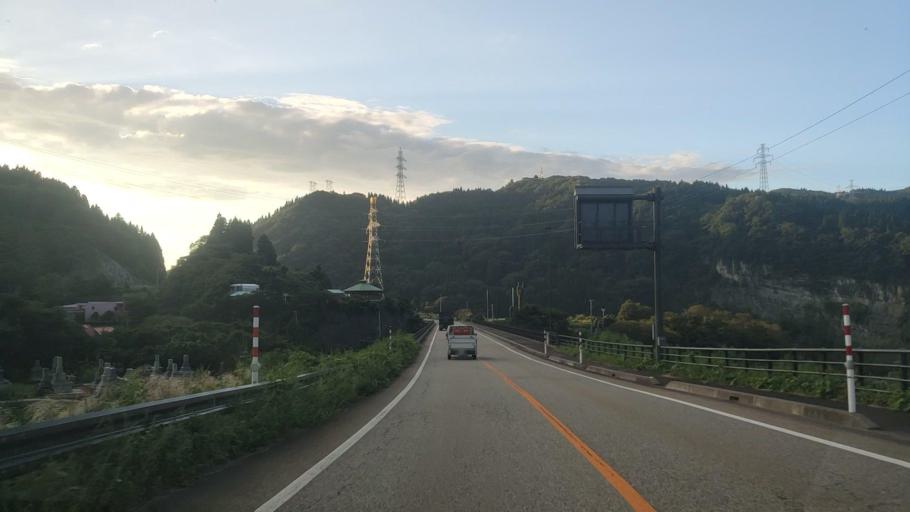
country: JP
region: Toyama
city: Nanto-shi
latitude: 36.5623
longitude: 137.0068
